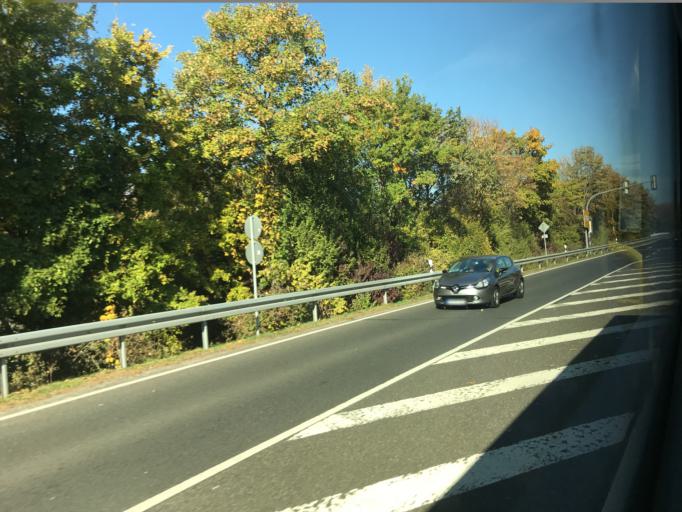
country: DE
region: Hesse
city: Liederbach
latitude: 50.1270
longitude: 8.4733
